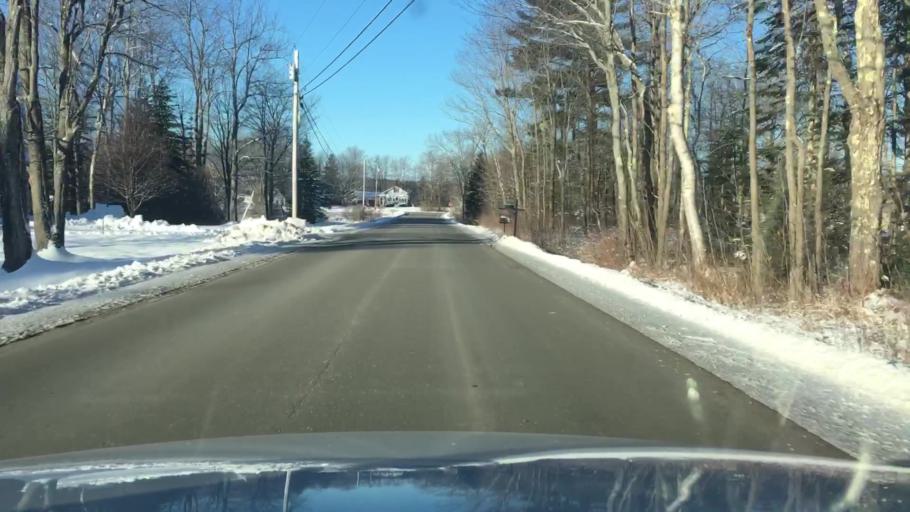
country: US
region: Maine
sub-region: Kennebec County
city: Belgrade
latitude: 44.4131
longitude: -69.8566
